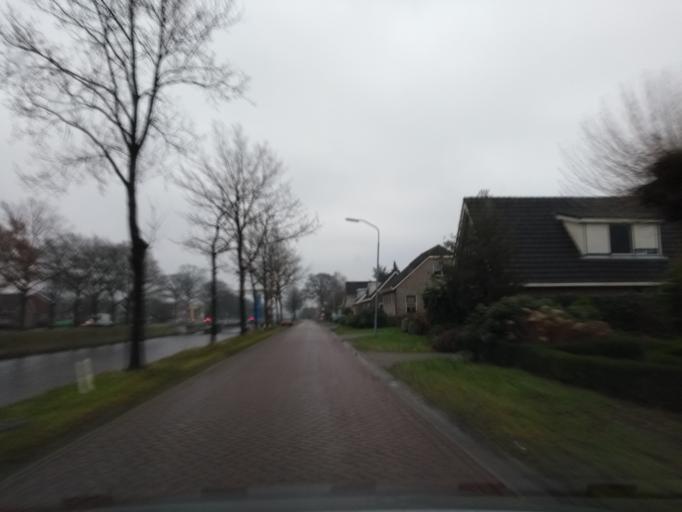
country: NL
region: Drenthe
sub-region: Gemeente Emmen
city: Klazienaveen
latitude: 52.7085
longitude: 6.9388
